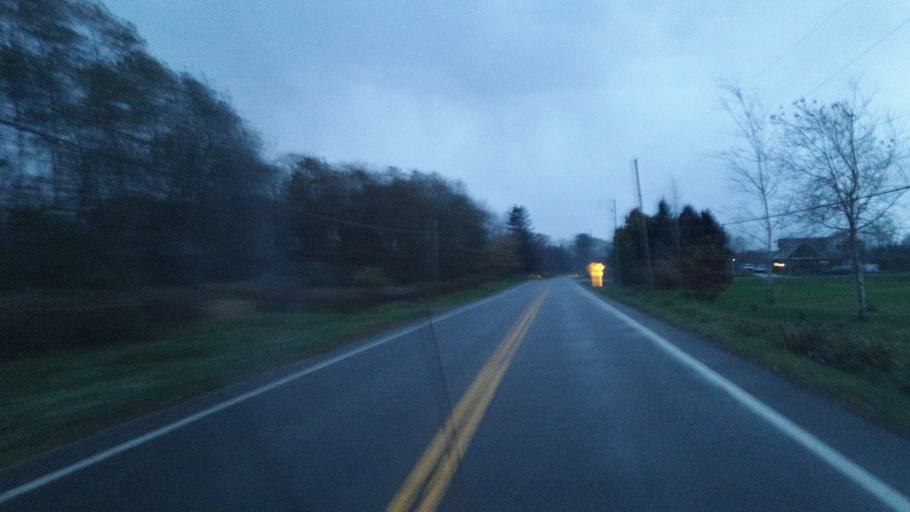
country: US
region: Ohio
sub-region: Portage County
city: Mantua
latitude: 41.3612
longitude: -81.2241
